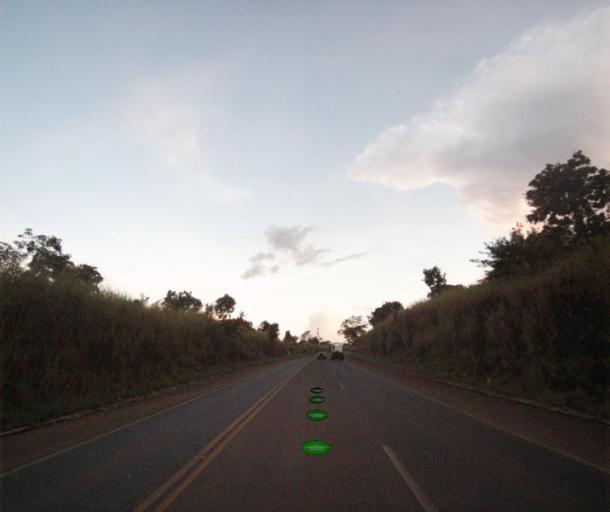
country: BR
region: Goias
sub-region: Uruacu
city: Uruacu
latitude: -14.5061
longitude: -49.1486
